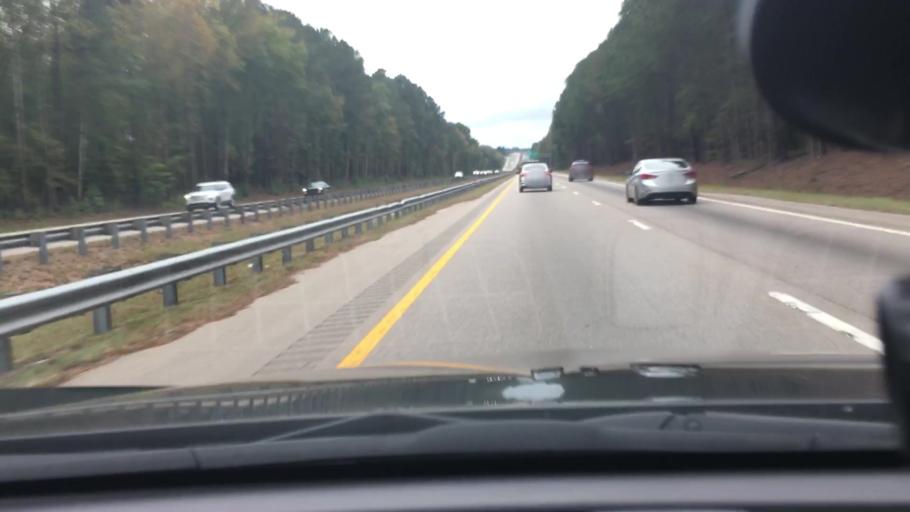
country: US
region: North Carolina
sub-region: Wake County
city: Wendell
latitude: 35.8165
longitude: -78.4002
